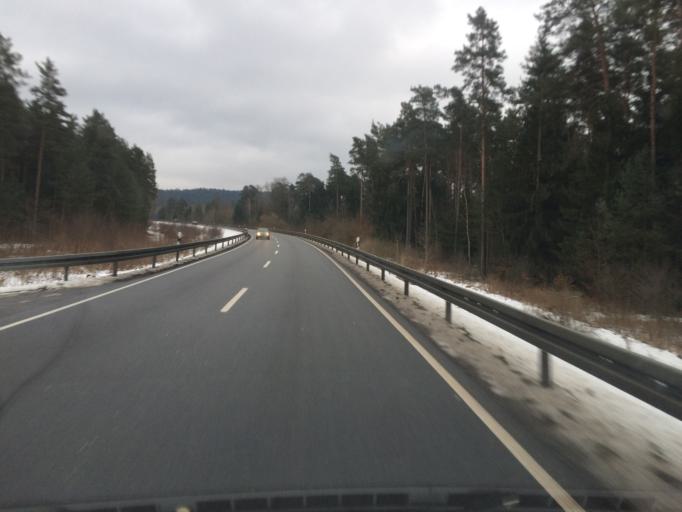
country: DE
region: Bavaria
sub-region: Upper Palatinate
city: Teublitz
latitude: 49.2194
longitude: 12.1169
